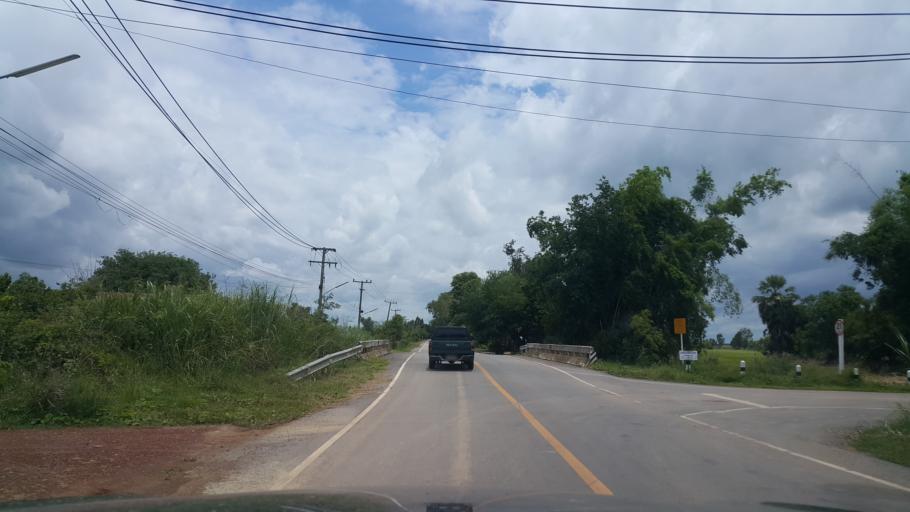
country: TH
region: Sukhothai
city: Kong Krailat
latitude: 16.9345
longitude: 99.9349
